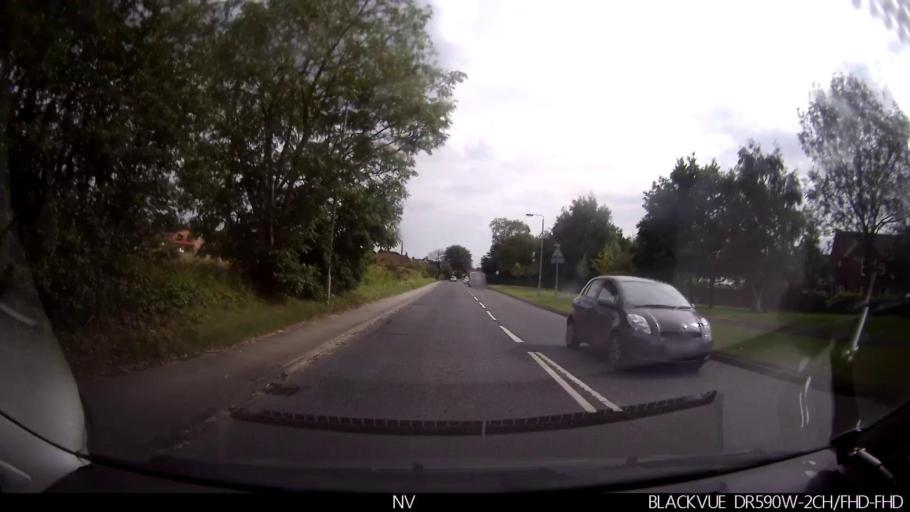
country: GB
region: England
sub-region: City of York
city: Huntington
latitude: 54.0090
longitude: -1.0541
